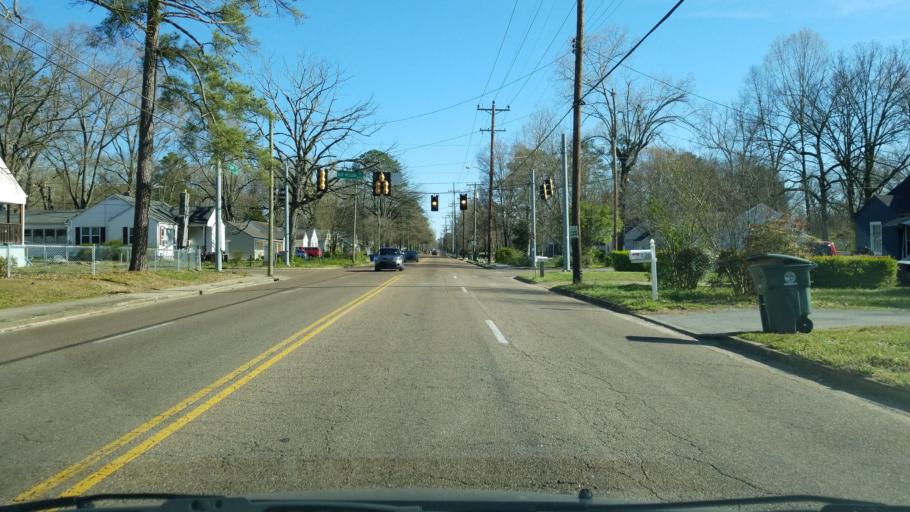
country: US
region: Tennessee
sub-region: Hamilton County
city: East Ridge
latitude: 35.0162
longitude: -85.2265
